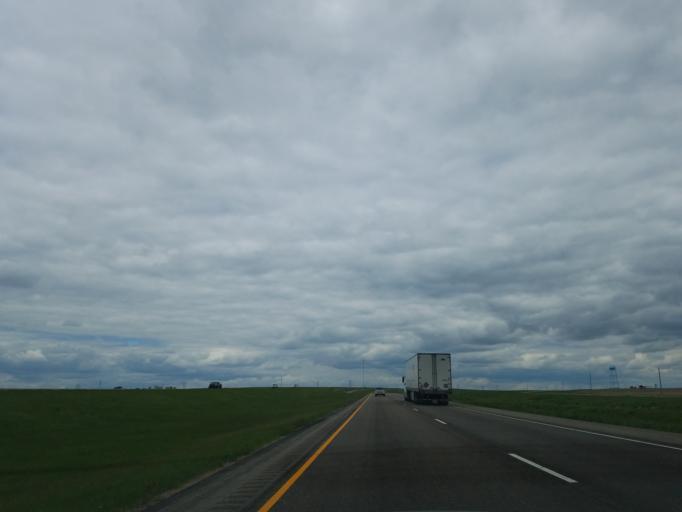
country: US
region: North Dakota
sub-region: Kidder County
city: Steele
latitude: 46.8467
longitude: -100.2434
